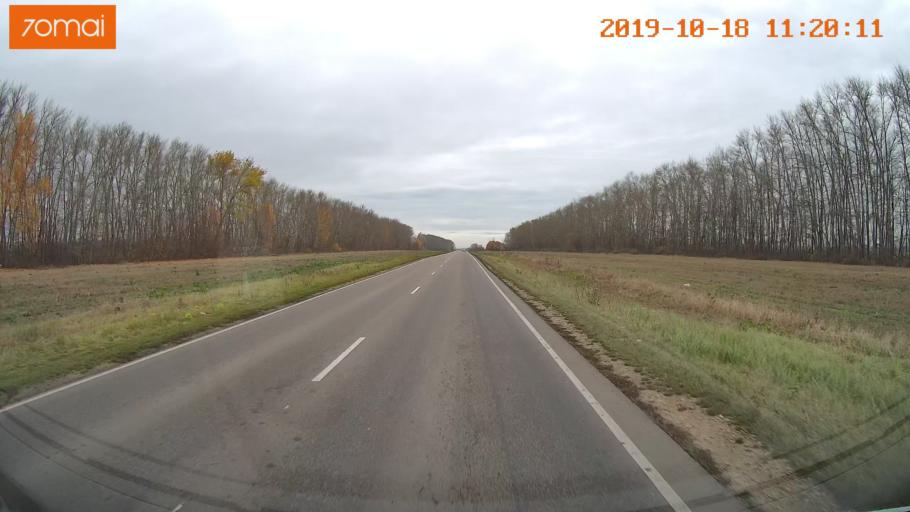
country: RU
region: Tula
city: Kimovsk
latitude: 54.0566
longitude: 38.5573
